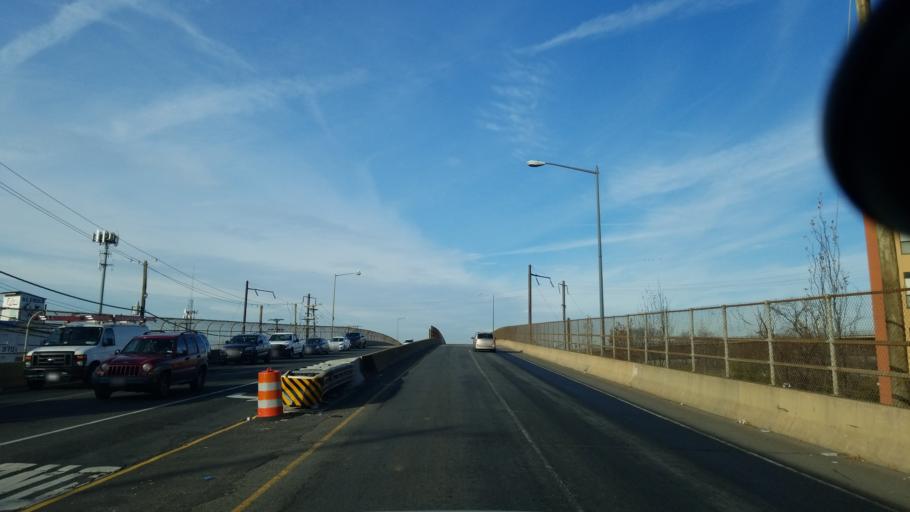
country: US
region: Maryland
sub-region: Prince George's County
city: Fairmount Heights
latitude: 38.8954
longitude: -76.9496
